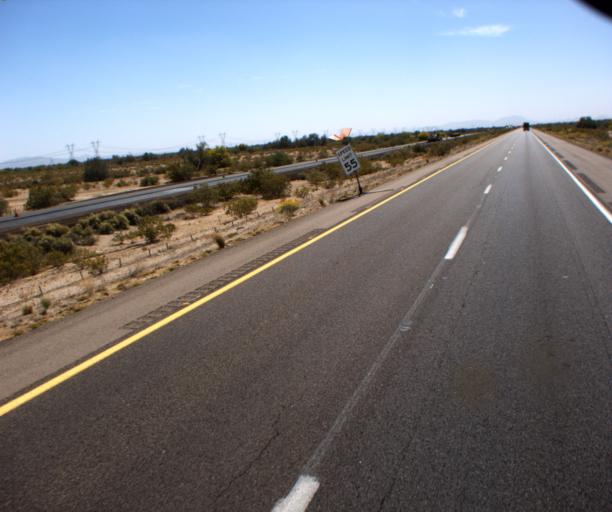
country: US
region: Arizona
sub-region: Maricopa County
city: Gila Bend
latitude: 33.0100
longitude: -112.6548
